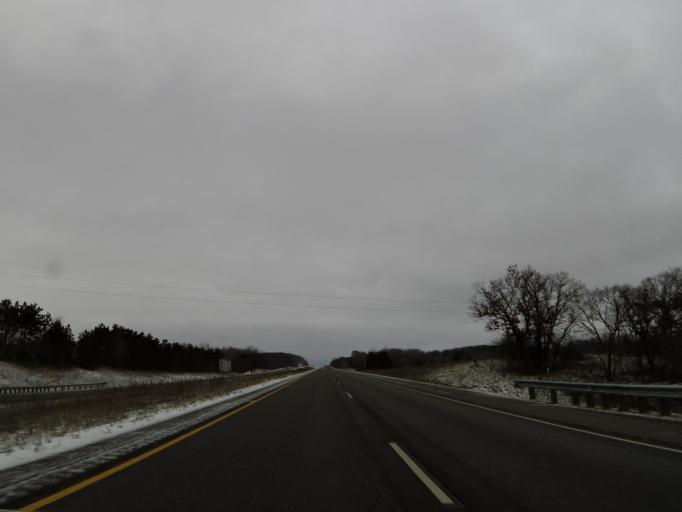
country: US
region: Wisconsin
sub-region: Eau Claire County
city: Eau Claire
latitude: 44.7880
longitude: -91.5458
